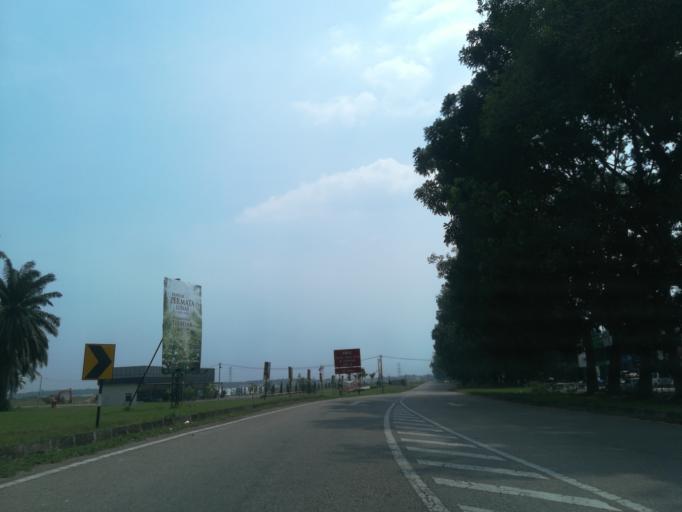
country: MY
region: Penang
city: Tasek Glugor
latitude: 5.4434
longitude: 100.5375
